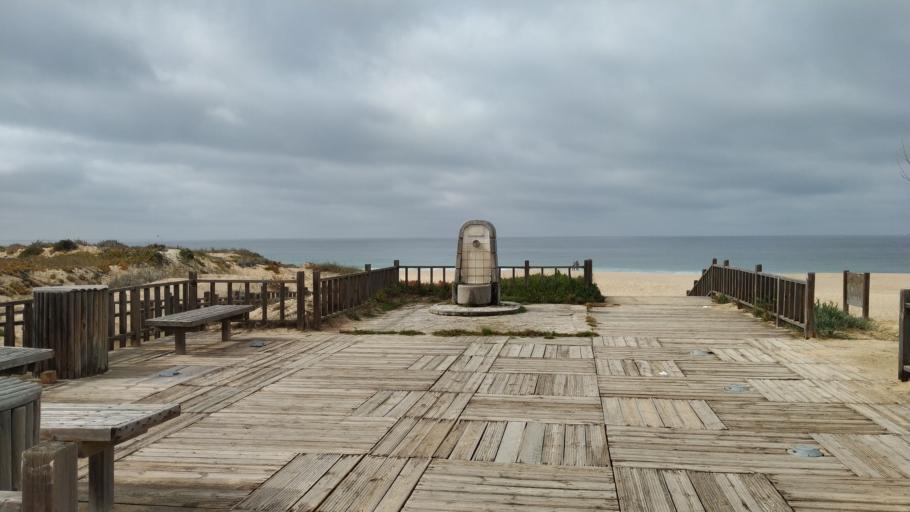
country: PT
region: Setubal
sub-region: Santiago do Cacem
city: Santo Andre
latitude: 38.1290
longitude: -8.7925
